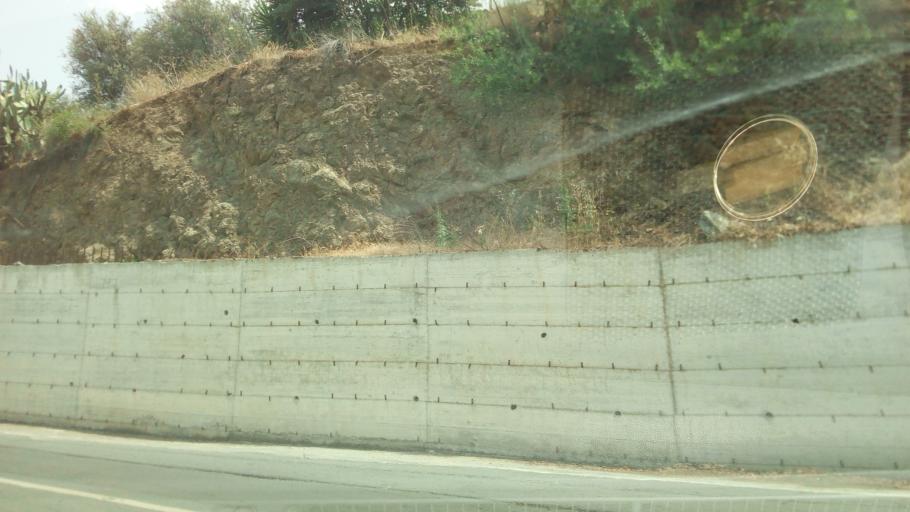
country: CY
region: Limassol
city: Parekklisha
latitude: 34.8390
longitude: 33.1860
